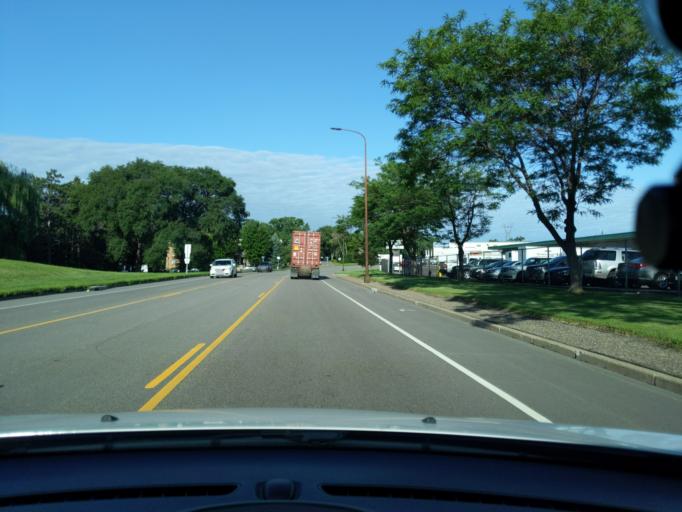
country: US
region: Minnesota
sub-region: Ramsey County
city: Falcon Heights
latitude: 44.9665
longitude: -93.1474
